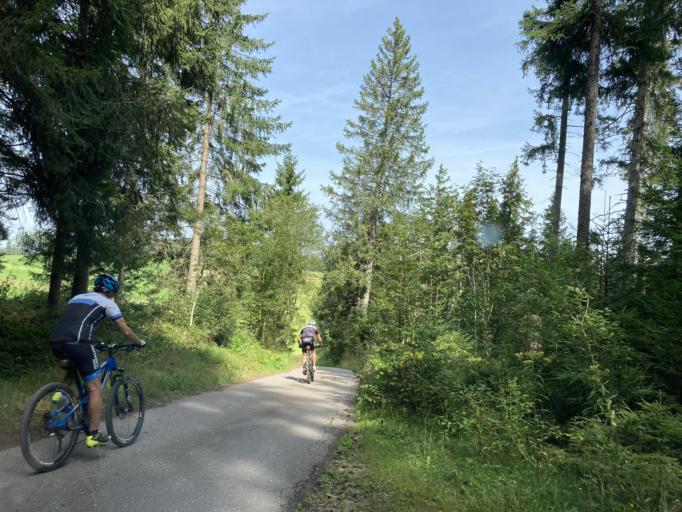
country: DE
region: Baden-Wuerttemberg
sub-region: Freiburg Region
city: Triberg im Schwarzwald
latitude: 48.1133
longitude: 8.2821
